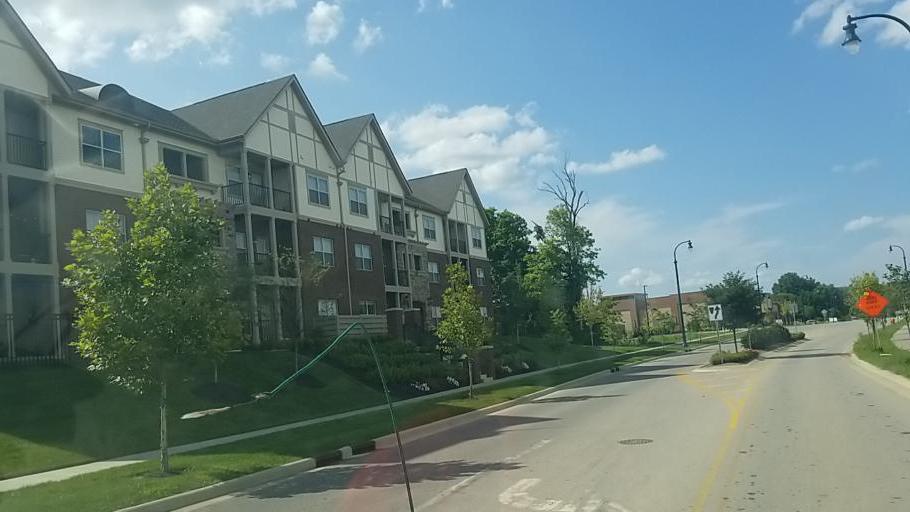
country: US
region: Ohio
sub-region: Franklin County
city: Westerville
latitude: 40.1428
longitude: -82.9561
